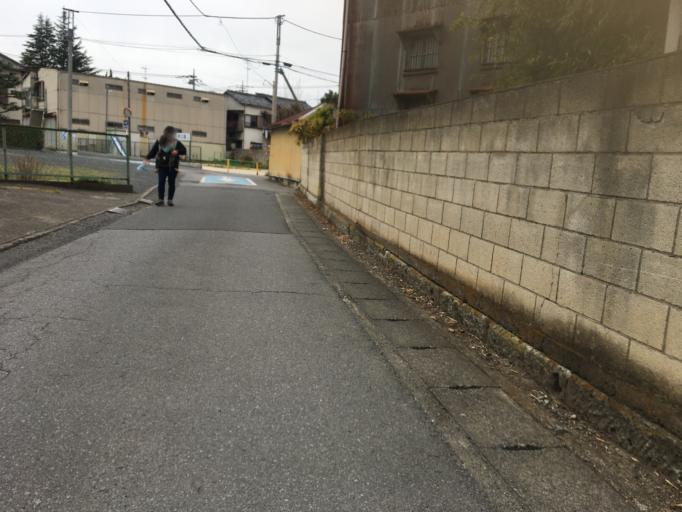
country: JP
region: Saitama
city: Kazo
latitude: 36.1230
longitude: 139.6027
